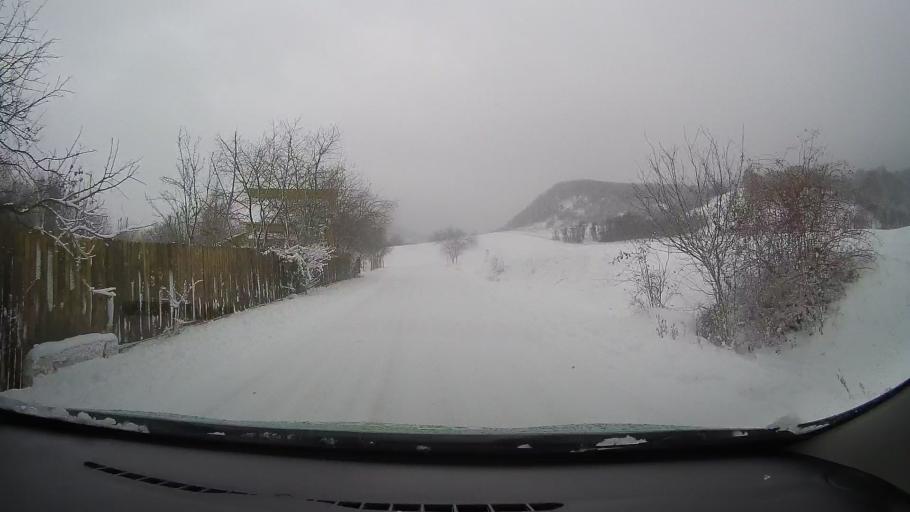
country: RO
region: Hunedoara
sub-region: Comuna Carjiti
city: Carjiti
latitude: 45.8430
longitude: 22.8332
